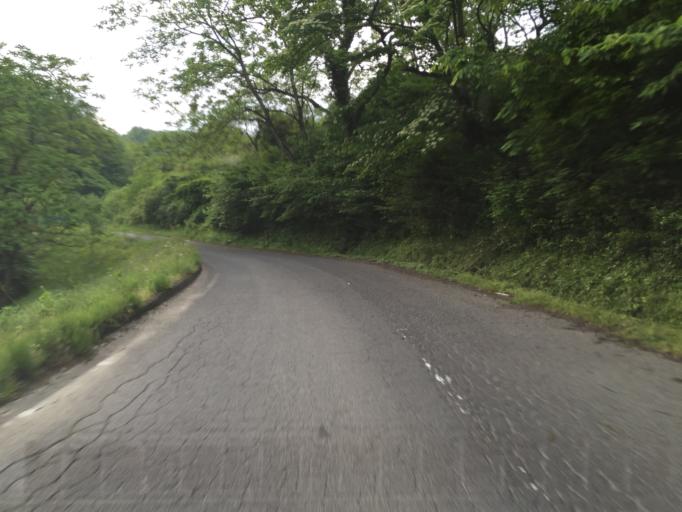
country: JP
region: Fukushima
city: Yanagawamachi-saiwaicho
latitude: 37.8993
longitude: 140.6626
